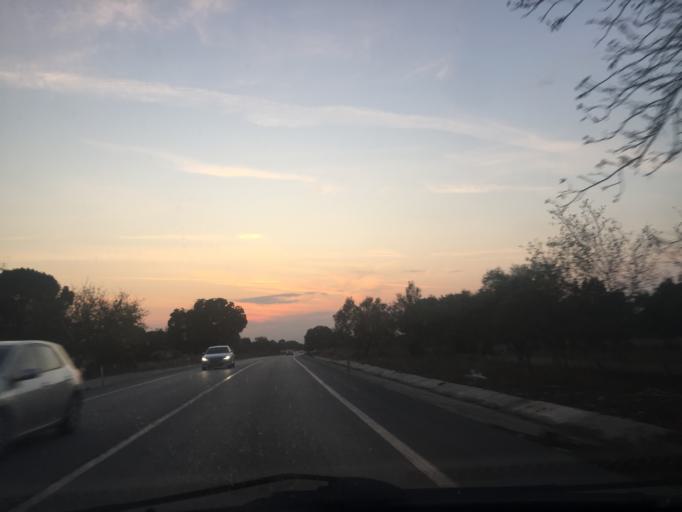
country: TR
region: Canakkale
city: Bayramic
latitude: 39.8114
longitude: 26.5637
